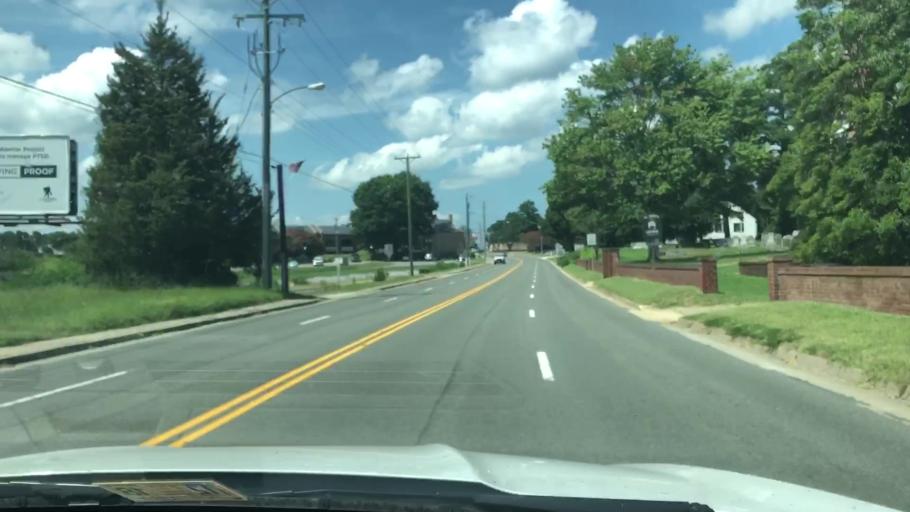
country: US
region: Virginia
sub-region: Richmond County
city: Warsaw
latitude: 37.9573
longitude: -76.7548
